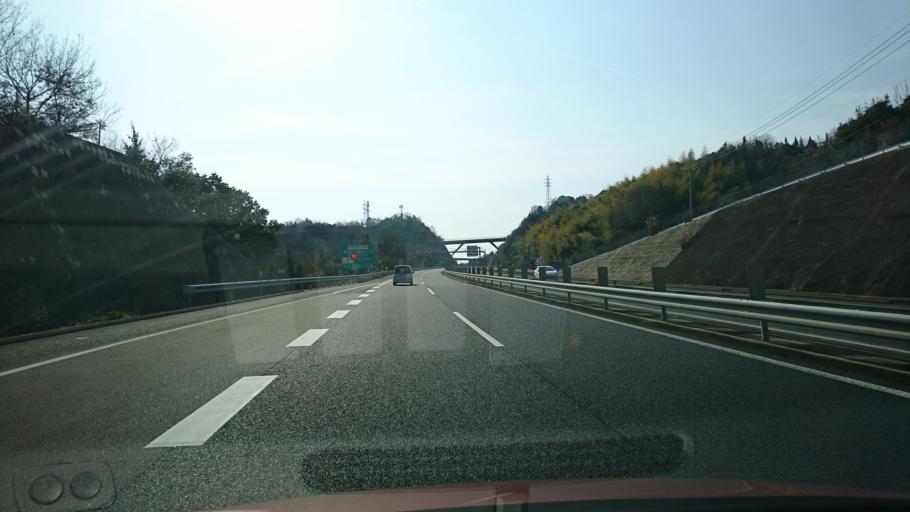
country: JP
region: Hiroshima
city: Onomichi
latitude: 34.4267
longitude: 133.2193
